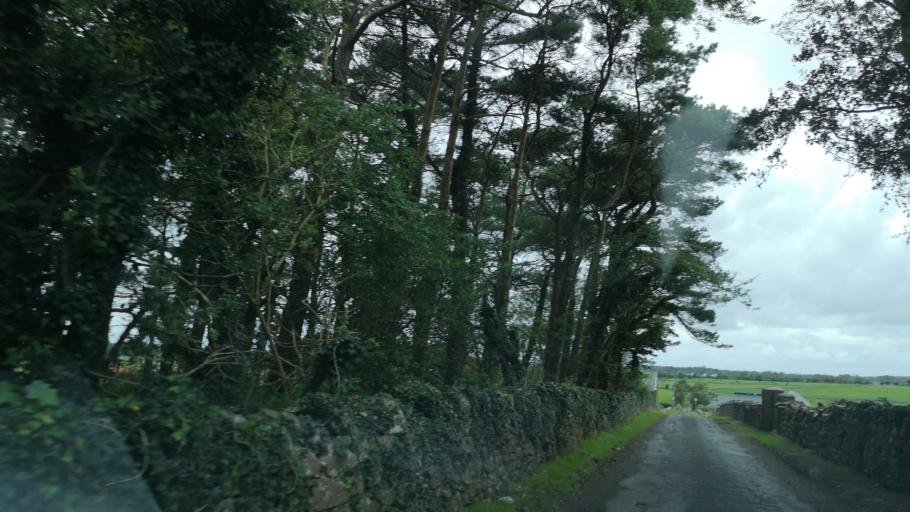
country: IE
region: Connaught
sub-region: County Galway
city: Athenry
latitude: 53.3125
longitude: -8.7456
